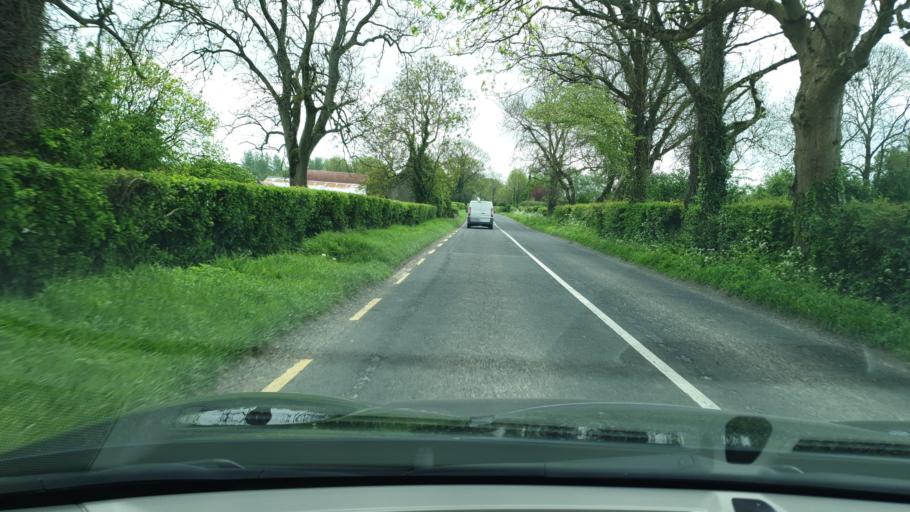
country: IE
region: Leinster
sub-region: An Mhi
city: Navan
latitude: 53.7172
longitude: -6.6967
